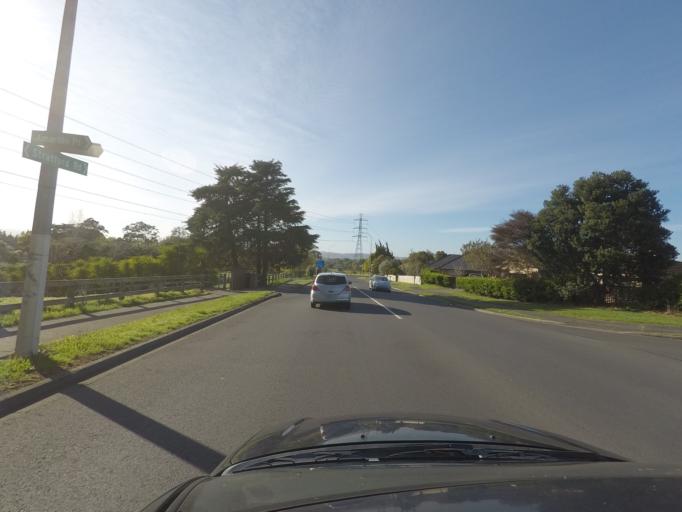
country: NZ
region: Auckland
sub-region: Auckland
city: Takanini
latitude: -37.0146
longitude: 174.9200
